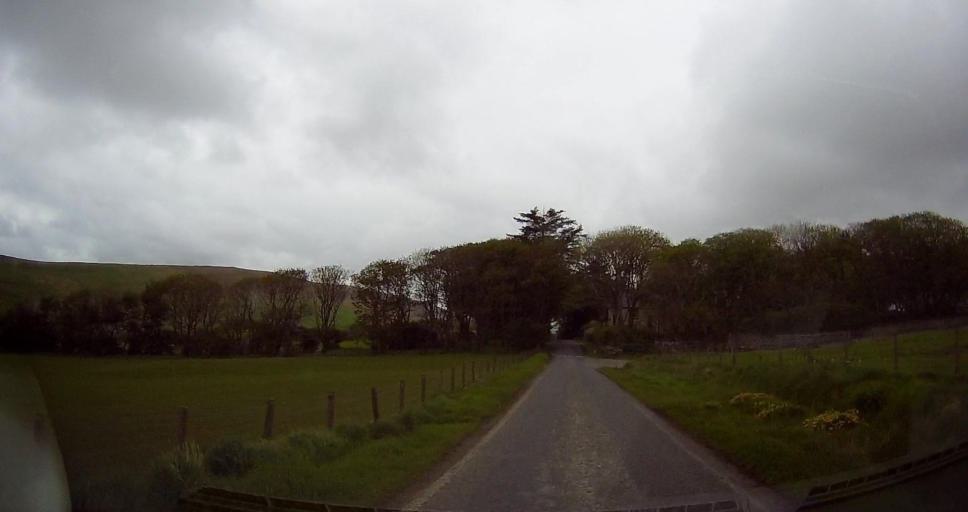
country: GB
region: Scotland
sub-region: Shetland Islands
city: Lerwick
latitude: 60.2719
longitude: -1.2863
